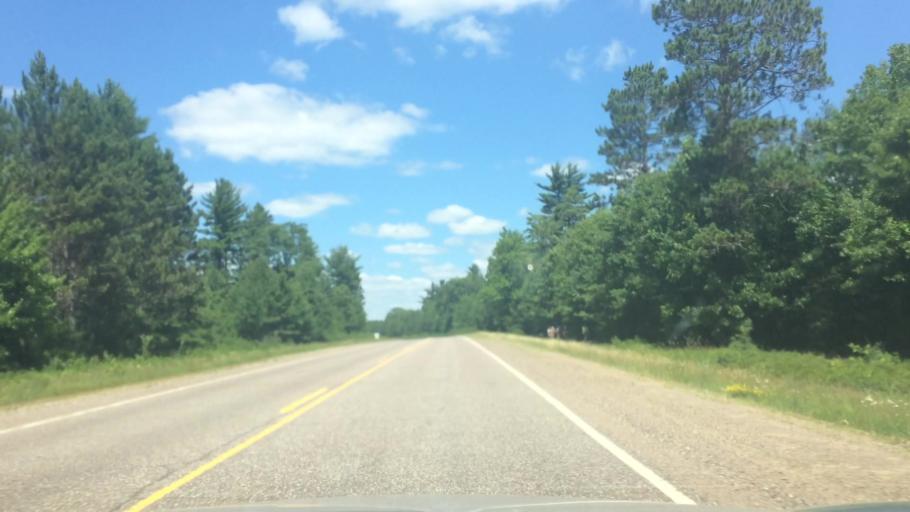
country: US
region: Wisconsin
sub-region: Vilas County
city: Lac du Flambeau
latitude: 46.0734
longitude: -89.6441
